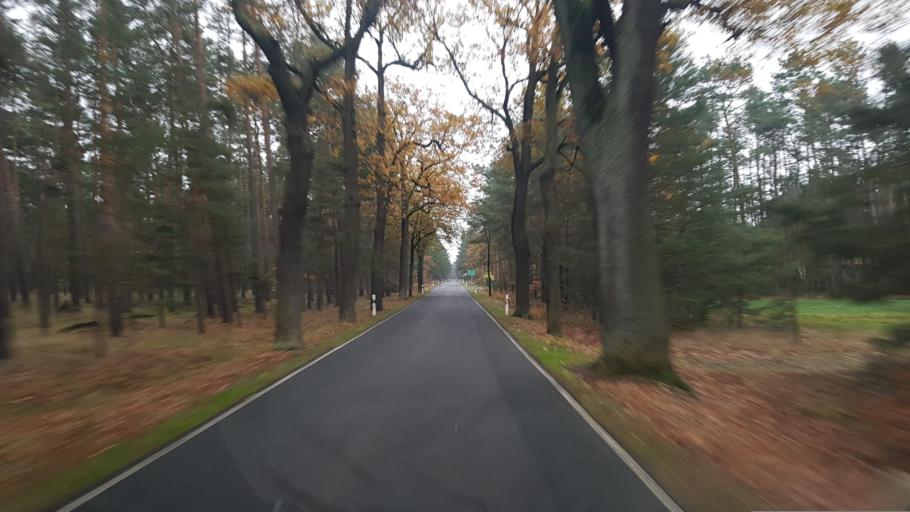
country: DE
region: Brandenburg
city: Ruhland
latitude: 51.4325
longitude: 13.8779
